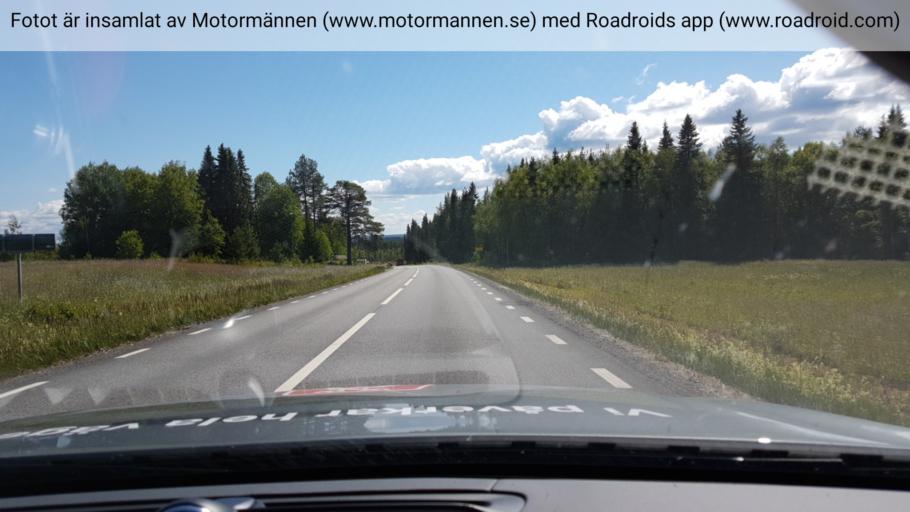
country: SE
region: Jaemtland
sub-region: Stroemsunds Kommun
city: Stroemsund
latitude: 63.8149
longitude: 15.5197
